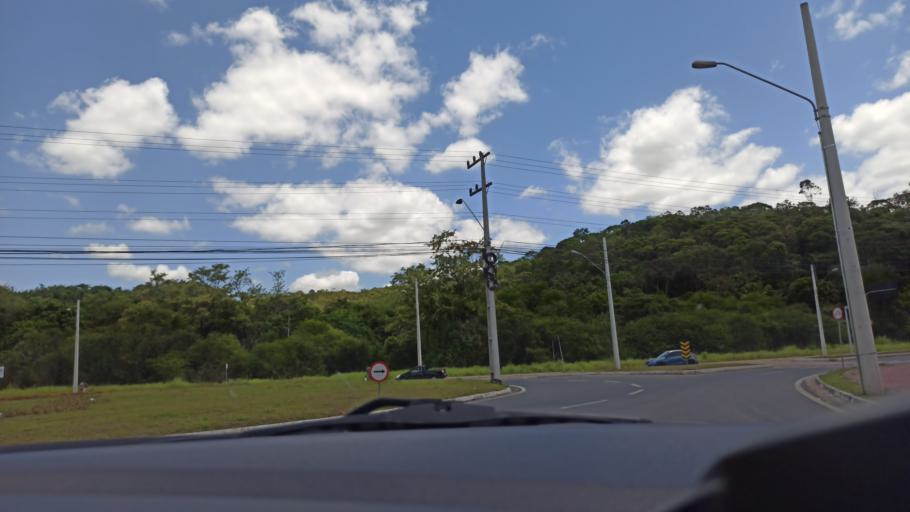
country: BR
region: Santa Catarina
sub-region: Pomerode
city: Pomerode
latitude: -26.7973
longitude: -49.0865
